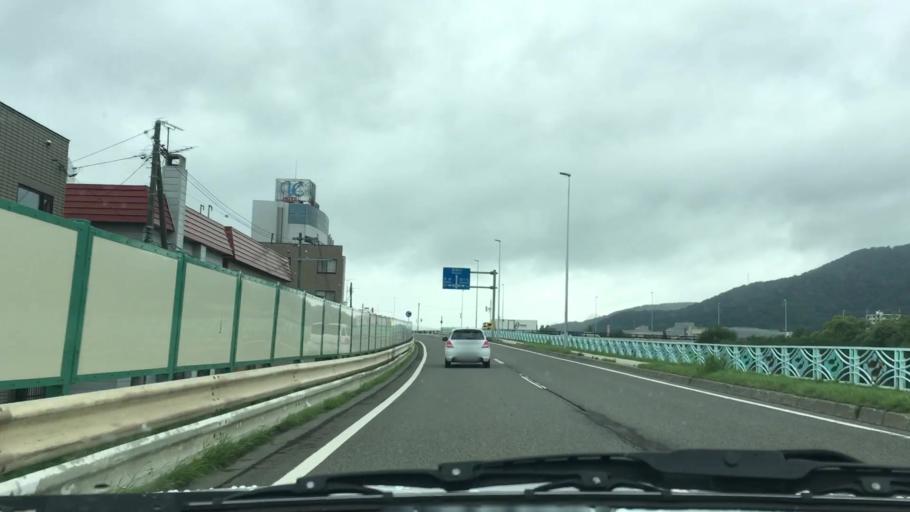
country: JP
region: Hokkaido
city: Sapporo
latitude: 43.0366
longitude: 141.3574
